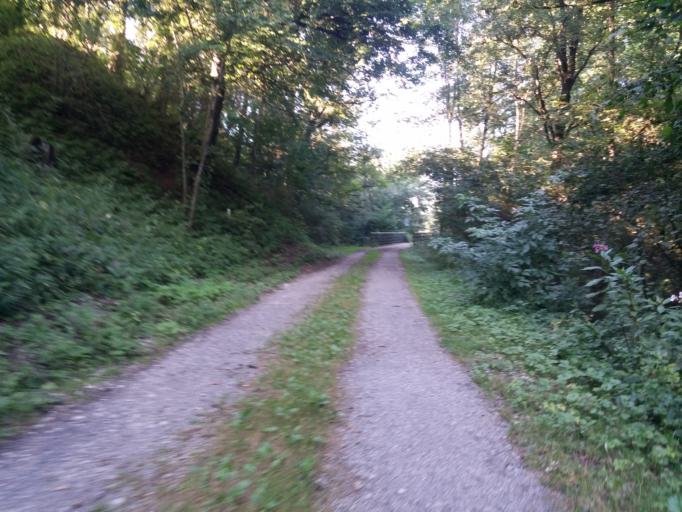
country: DE
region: Bavaria
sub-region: Swabia
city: Lautrach
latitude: 47.8969
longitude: 10.1210
